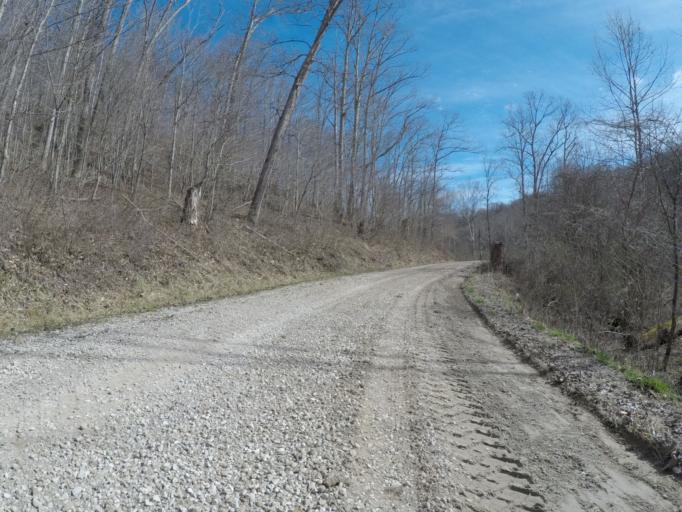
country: US
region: West Virginia
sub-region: Wayne County
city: Ceredo
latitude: 38.3424
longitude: -82.5398
